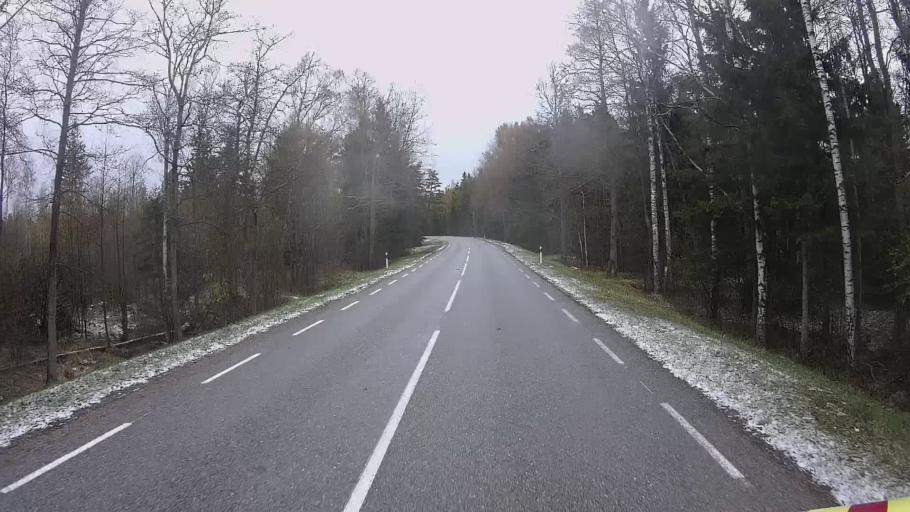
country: EE
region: Hiiumaa
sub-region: Kaerdla linn
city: Kardla
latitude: 59.0340
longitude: 22.6791
